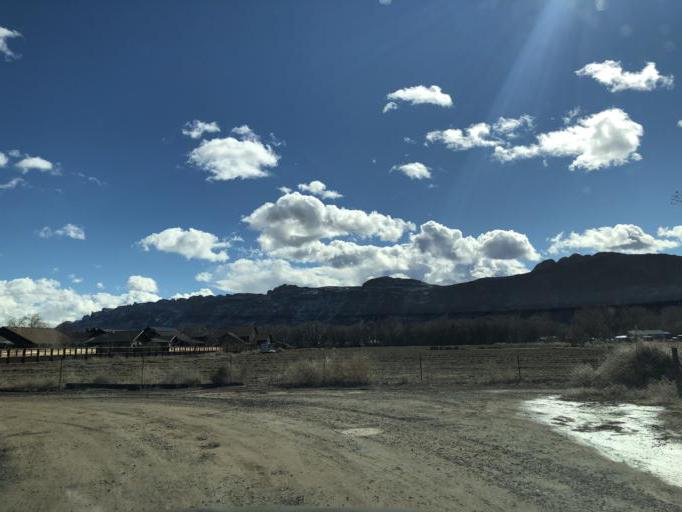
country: US
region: Utah
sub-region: Grand County
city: Moab
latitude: 38.5863
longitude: -109.5650
